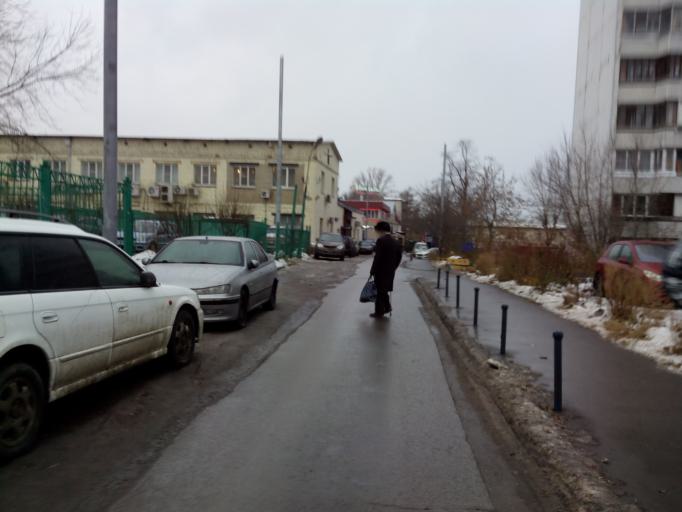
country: RU
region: Moscow
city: Ostankinskiy
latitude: 55.8248
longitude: 37.6260
